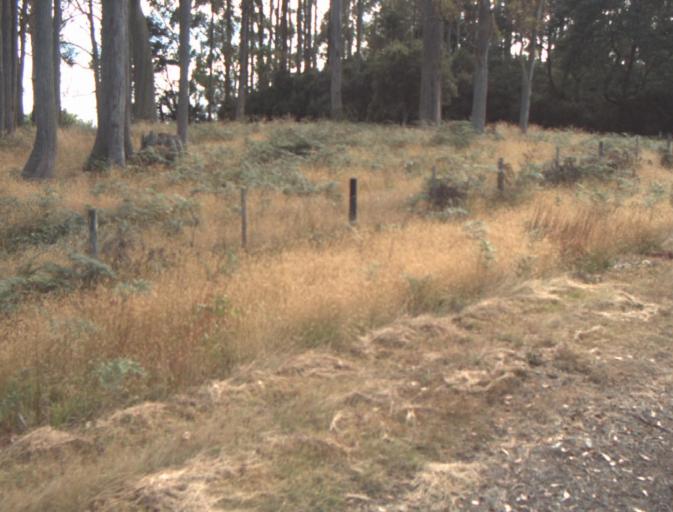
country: AU
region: Tasmania
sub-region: Launceston
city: Mayfield
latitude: -41.2914
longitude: 147.2101
